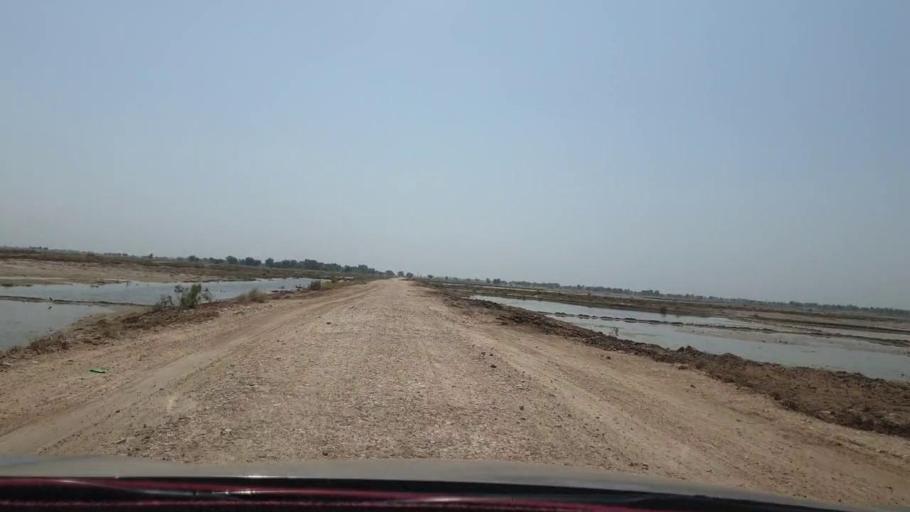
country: PK
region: Sindh
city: Kambar
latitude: 27.5780
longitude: 67.8783
